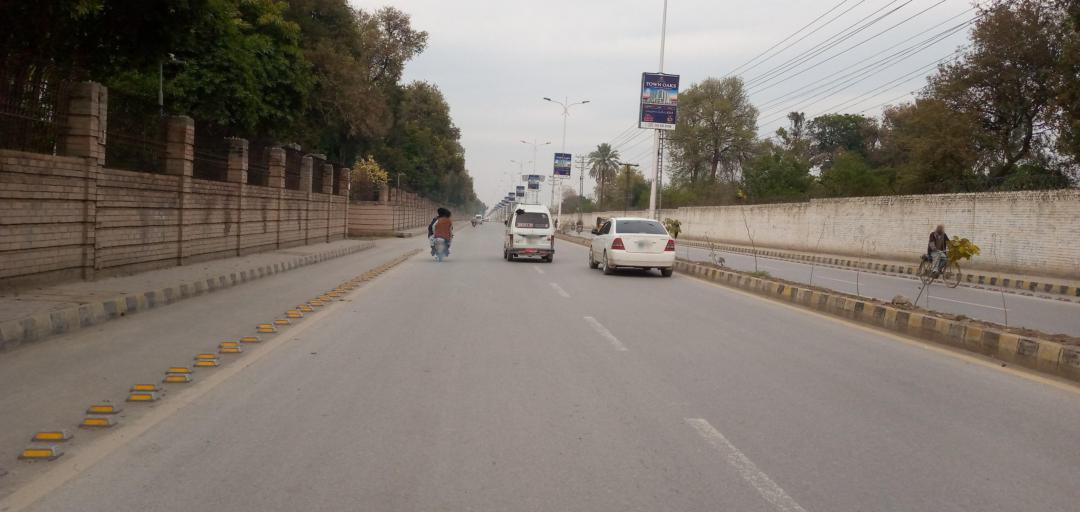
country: PK
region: Khyber Pakhtunkhwa
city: Peshawar
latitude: 34.0002
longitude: 71.4885
